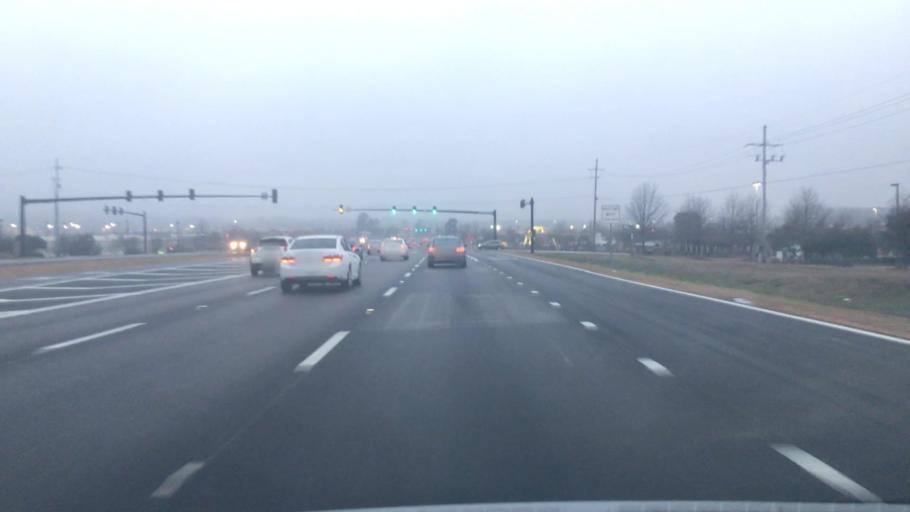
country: US
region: Mississippi
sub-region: Rankin County
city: Flowood
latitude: 32.3424
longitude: -90.0578
